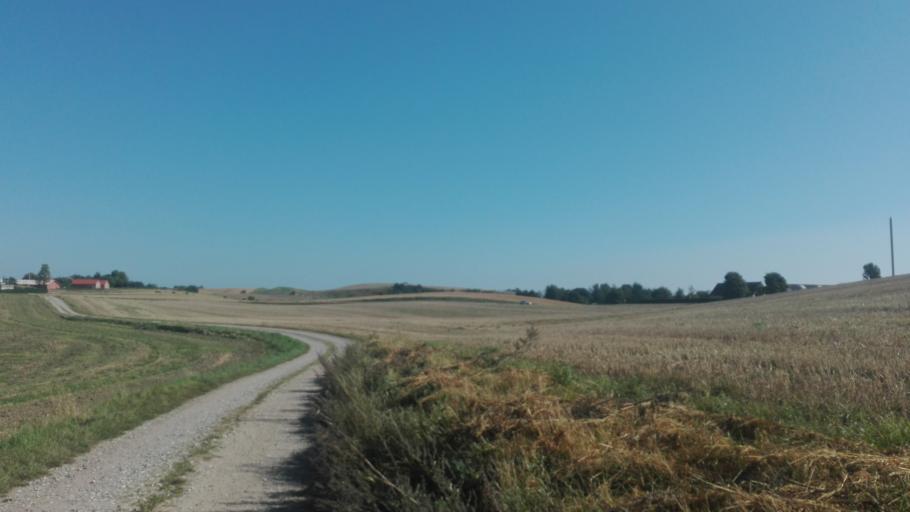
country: DK
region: Central Jutland
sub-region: Syddjurs Kommune
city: Ebeltoft
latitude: 56.2350
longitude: 10.7452
